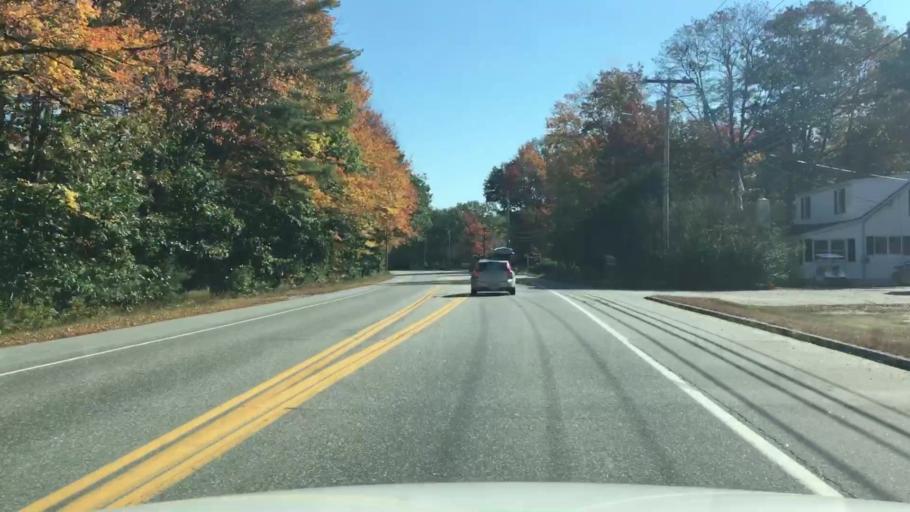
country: US
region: Maine
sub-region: Sagadahoc County
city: Topsham
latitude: 43.9536
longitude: -69.9973
